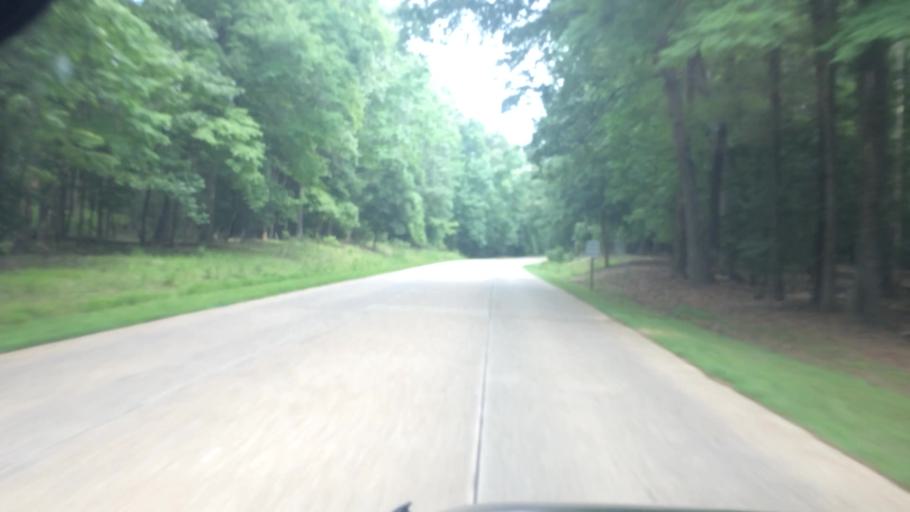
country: US
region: Virginia
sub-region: City of Williamsburg
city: Williamsburg
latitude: 37.2312
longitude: -76.6960
